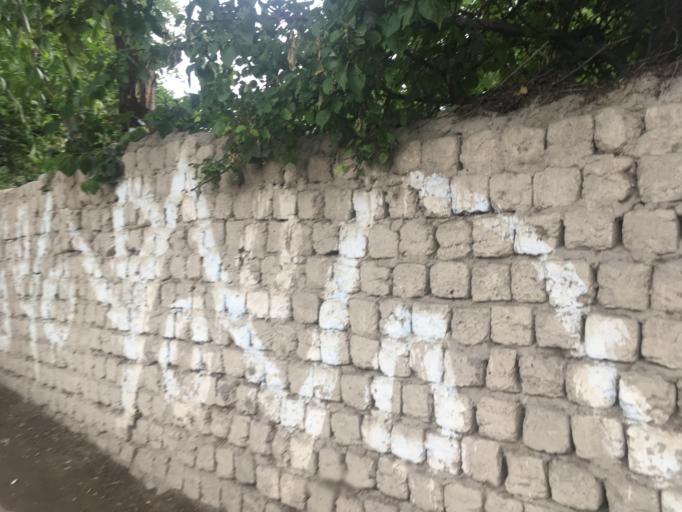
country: PK
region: Gilgit-Baltistan
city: Skardu
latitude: 35.2917
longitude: 75.6506
